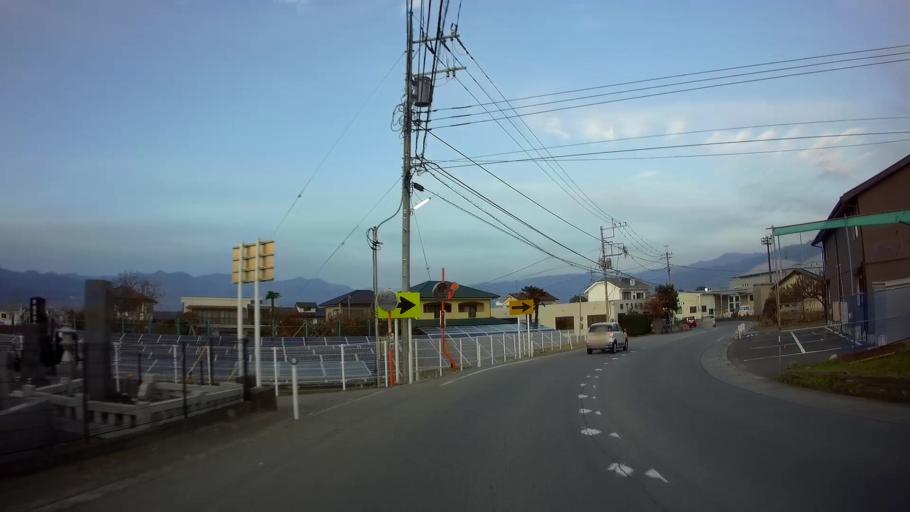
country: JP
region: Yamanashi
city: Isawa
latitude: 35.6482
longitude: 138.6877
